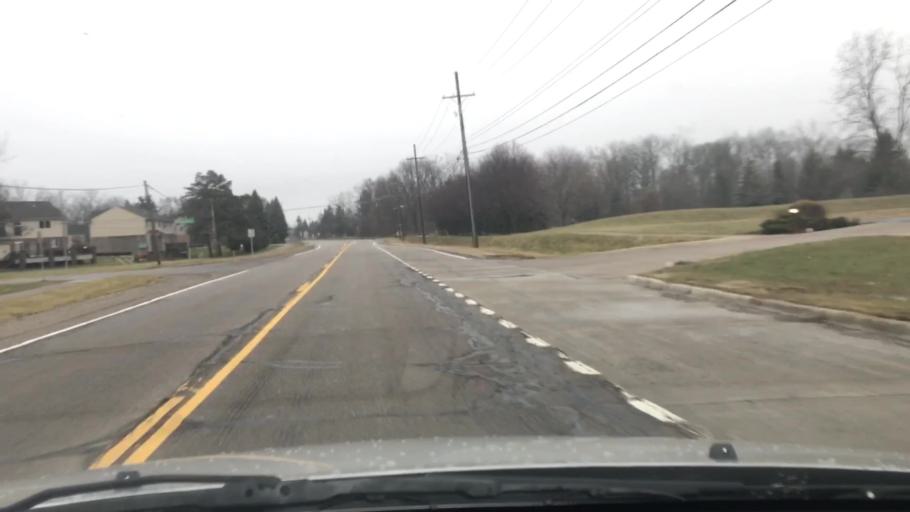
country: US
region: Michigan
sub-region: Oakland County
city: Troy
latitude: 42.6312
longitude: -83.1520
